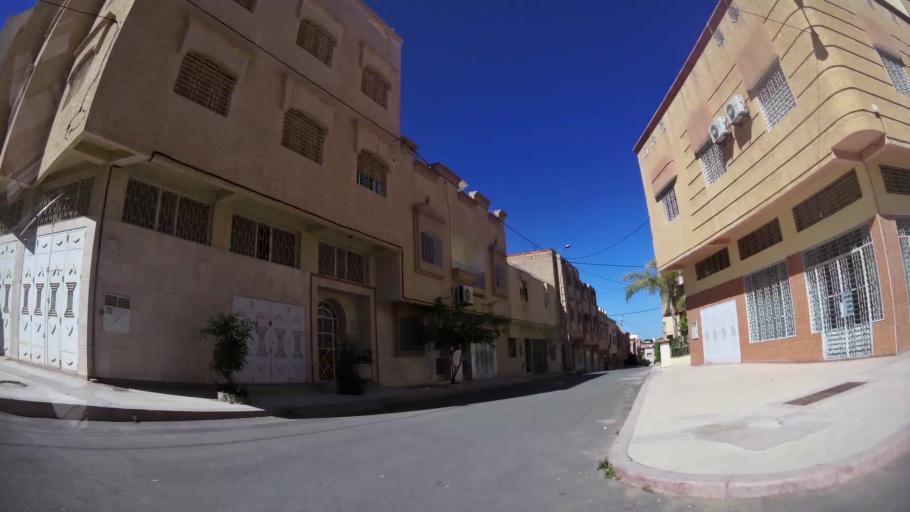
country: MA
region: Oriental
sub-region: Oujda-Angad
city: Oujda
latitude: 34.6556
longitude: -1.8881
